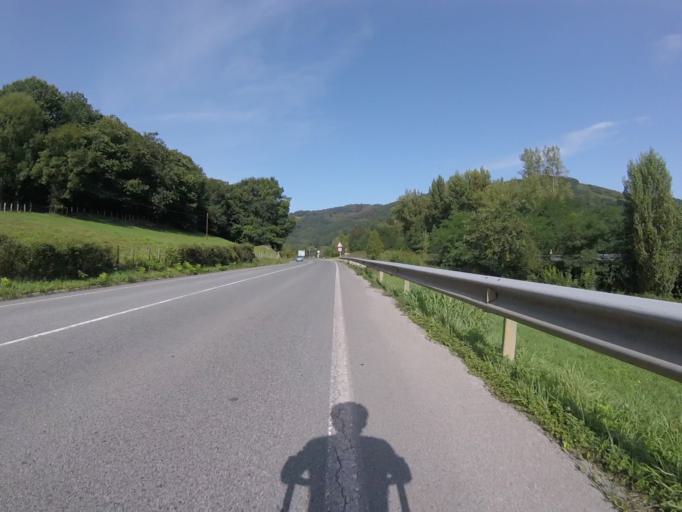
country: ES
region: Navarre
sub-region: Provincia de Navarra
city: Doneztebe
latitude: 43.1398
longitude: -1.5598
